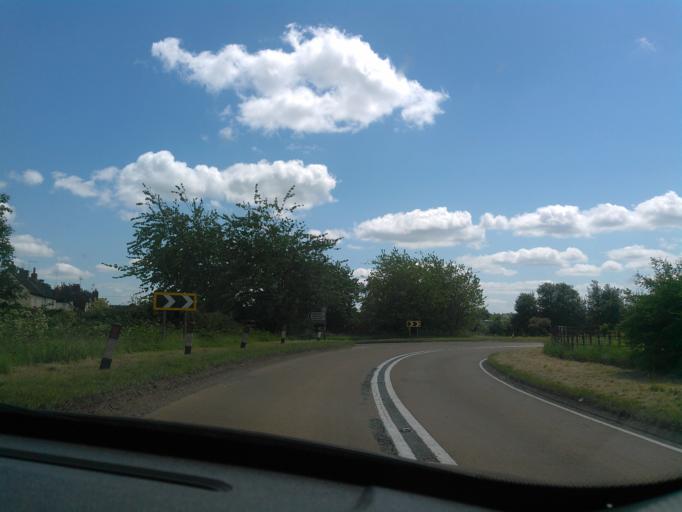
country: GB
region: England
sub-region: Shropshire
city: Prees
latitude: 52.8982
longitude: -2.6269
